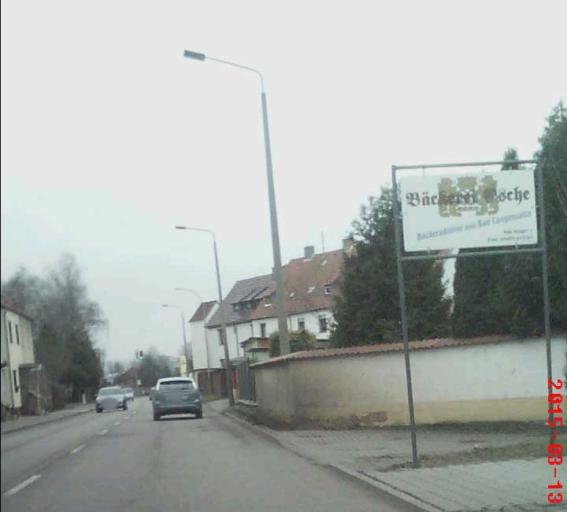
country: DE
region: Thuringia
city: Bad Langensalza
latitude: 51.1144
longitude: 10.6498
